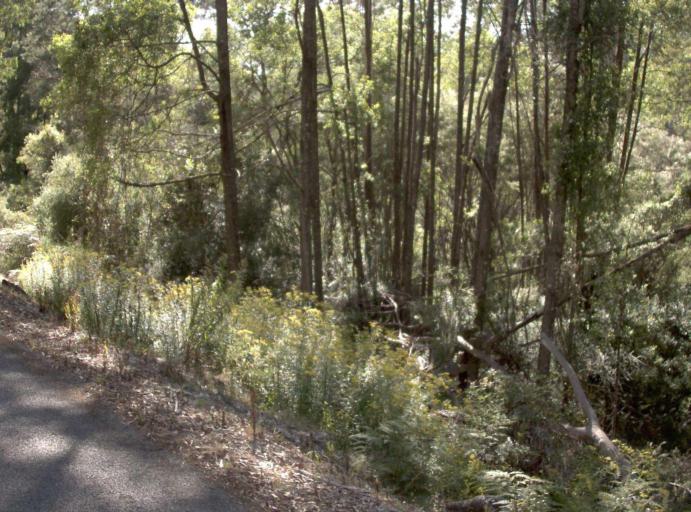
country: AU
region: Victoria
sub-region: East Gippsland
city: Lakes Entrance
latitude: -37.5046
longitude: 148.5350
